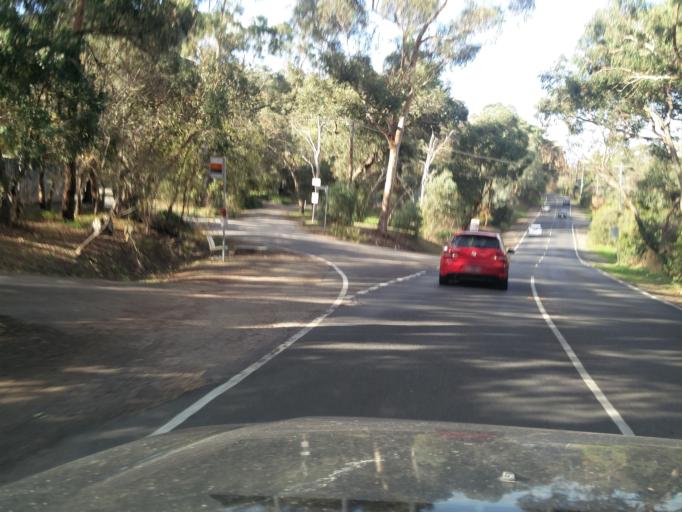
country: AU
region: Victoria
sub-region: Nillumbik
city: Eltham
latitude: -37.7255
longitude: 145.1548
